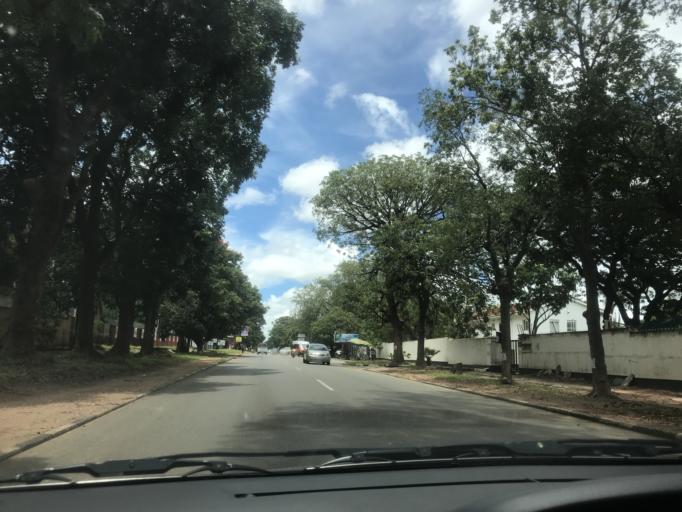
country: ZM
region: Lusaka
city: Lusaka
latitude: -15.4184
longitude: 28.3110
